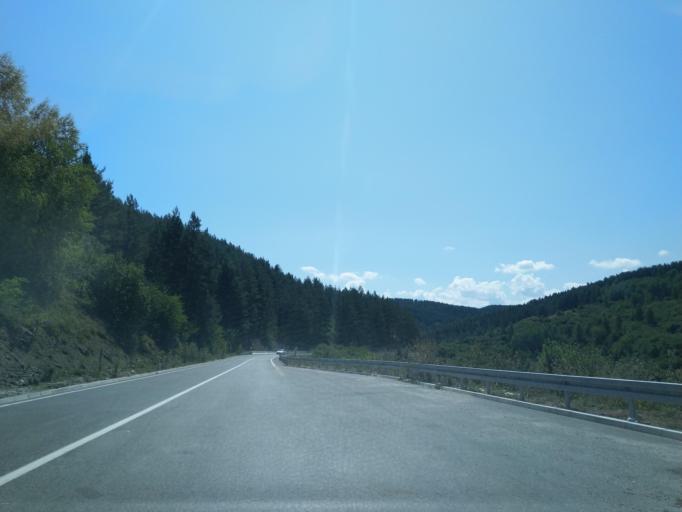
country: RS
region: Central Serbia
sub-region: Zlatiborski Okrug
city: Sjenica
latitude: 43.2861
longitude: 19.9451
